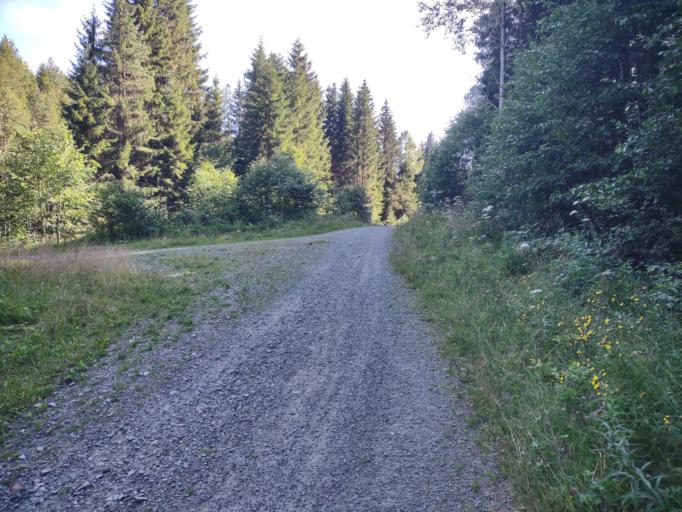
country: NO
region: Akershus
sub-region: Raelingen
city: Fjerdingby
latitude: 59.8681
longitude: 11.0128
